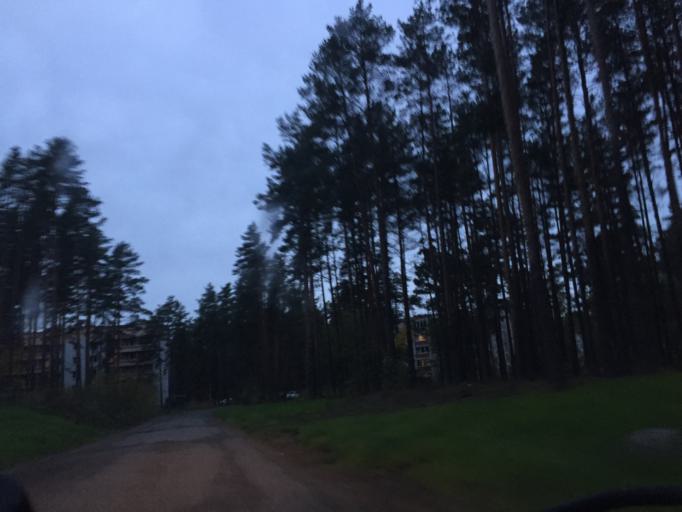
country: LV
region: Adazi
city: Adazi
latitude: 57.0896
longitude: 24.3625
